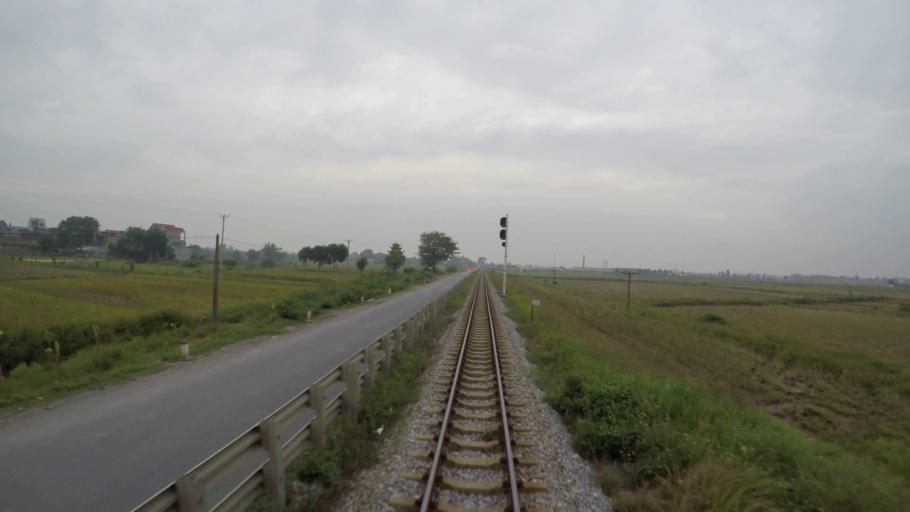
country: VN
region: Hung Yen
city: Ban Yen Nhan
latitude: 20.9716
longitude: 106.0985
